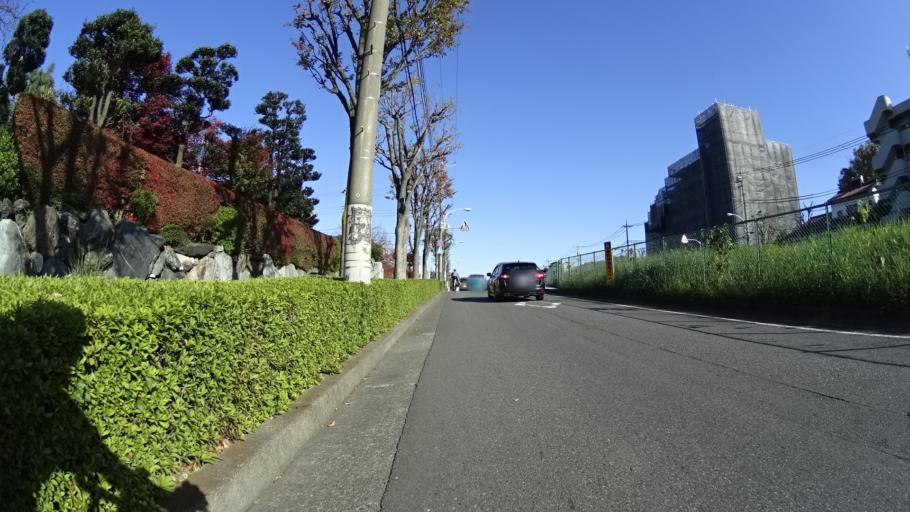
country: JP
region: Tokyo
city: Hino
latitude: 35.6089
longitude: 139.4276
